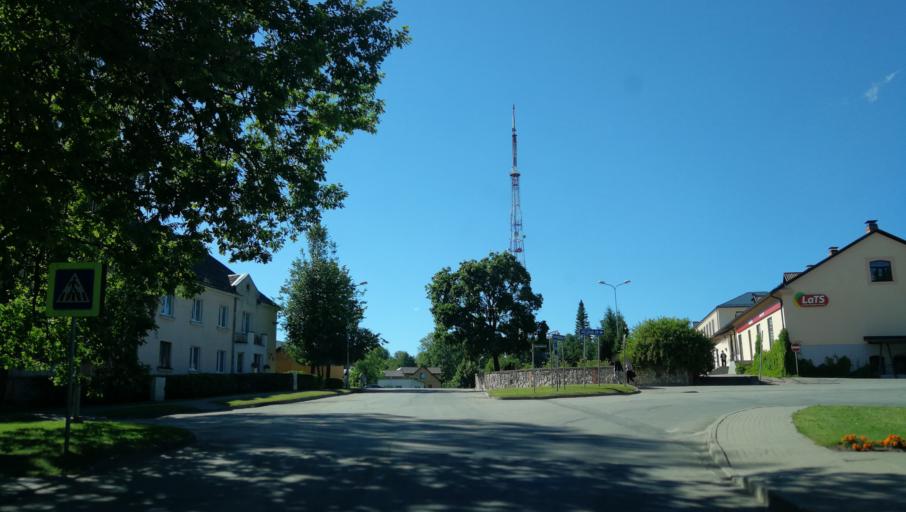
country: LV
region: Cesvaine
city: Cesvaine
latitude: 56.9682
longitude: 26.3072
